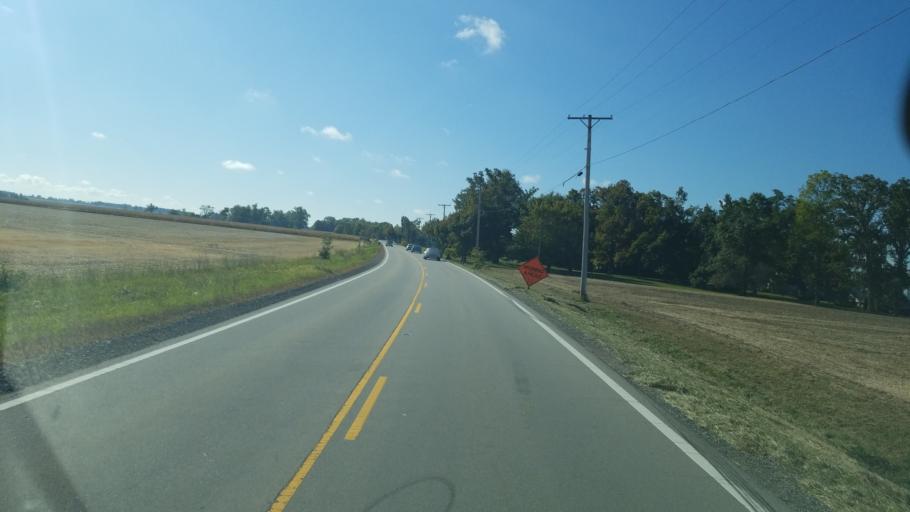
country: US
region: Ohio
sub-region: Fayette County
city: Washington Court House
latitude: 39.4619
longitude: -83.4895
